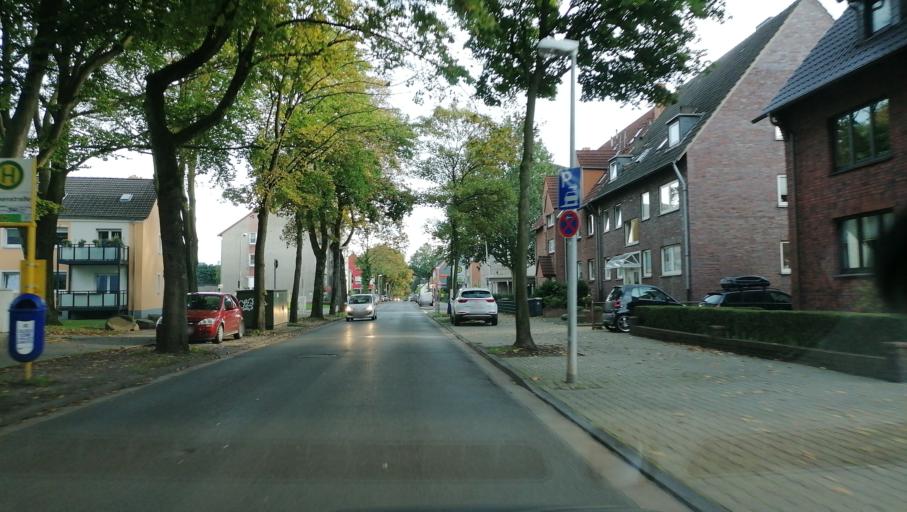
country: DE
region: North Rhine-Westphalia
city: Herten
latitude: 51.5756
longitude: 7.1094
